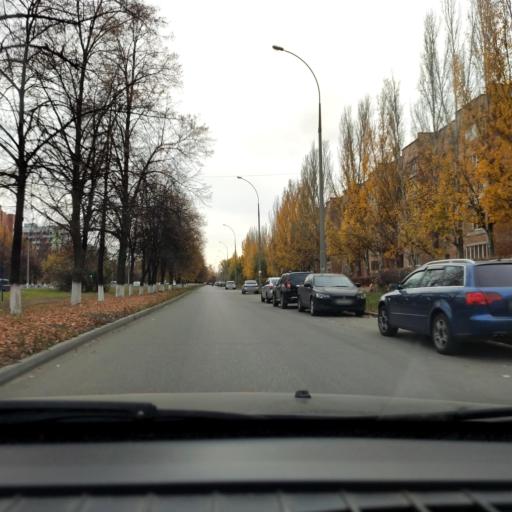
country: RU
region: Samara
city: Tol'yatti
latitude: 53.5230
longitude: 49.3107
